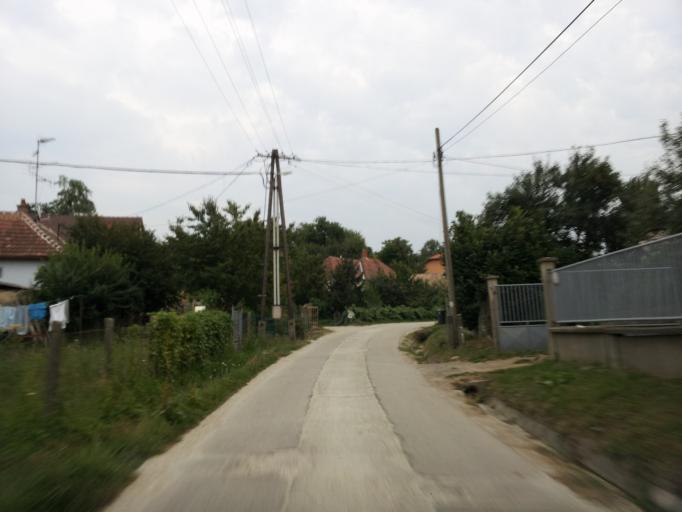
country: HU
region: Vas
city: Sarvar
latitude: 47.2427
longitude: 16.9674
